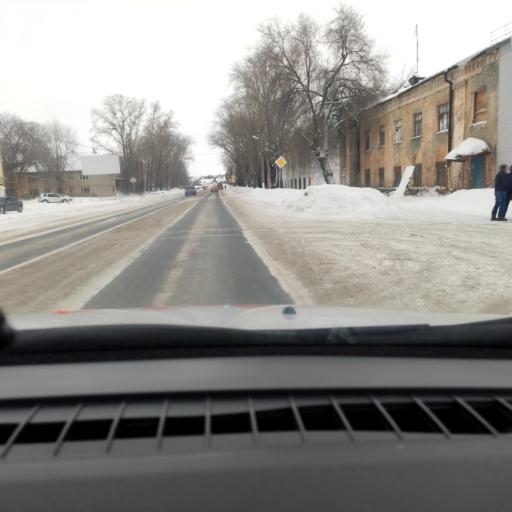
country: RU
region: Samara
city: Chapayevsk
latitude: 52.9515
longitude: 49.6889
